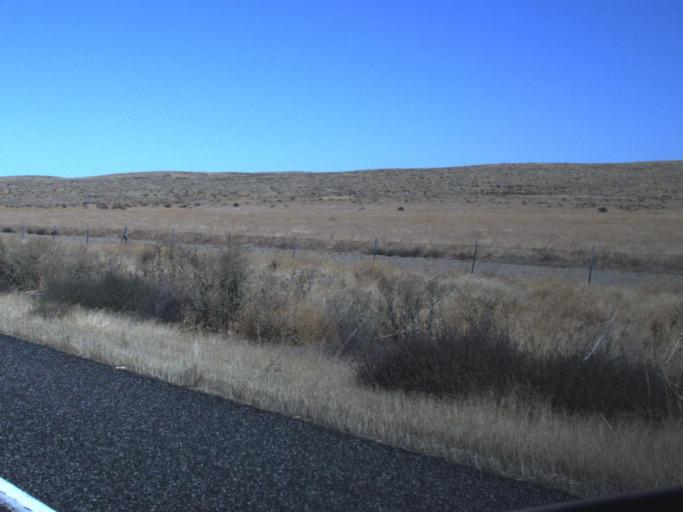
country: US
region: Washington
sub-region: Benton County
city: Benton City
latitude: 46.4888
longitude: -119.5876
